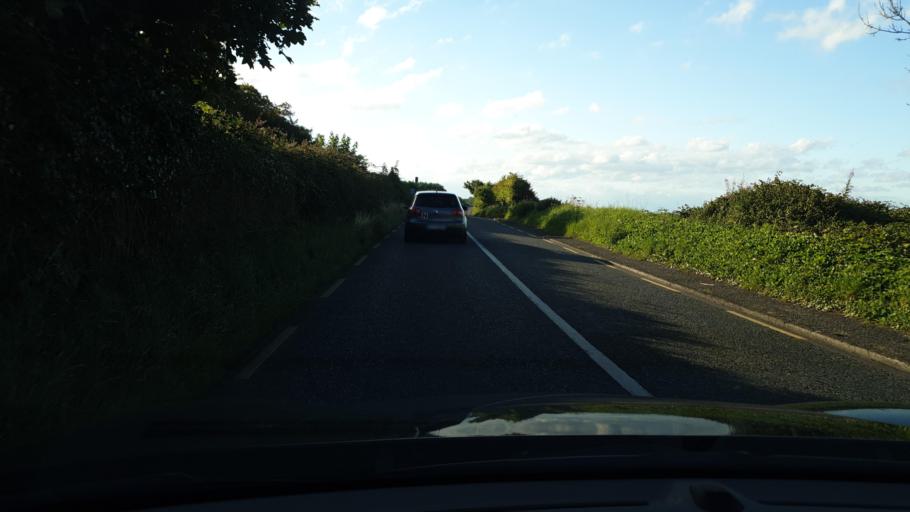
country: IE
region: Leinster
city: Balrothery
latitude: 53.5934
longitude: -6.1584
